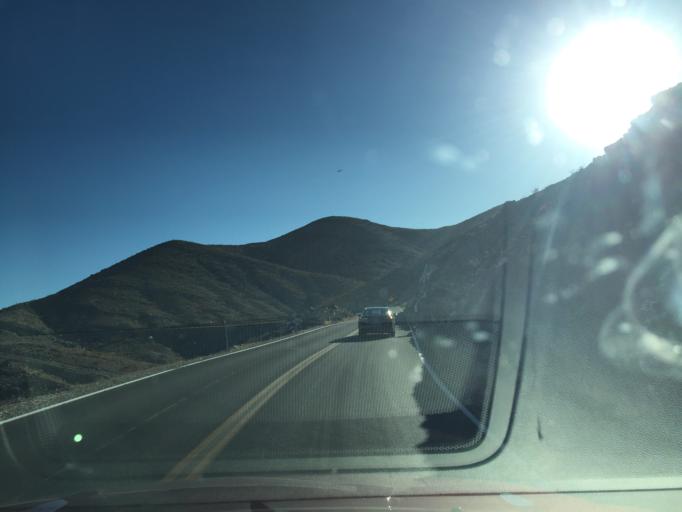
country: US
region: California
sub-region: Inyo County
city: Lone Pine
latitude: 36.3535
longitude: -117.5347
